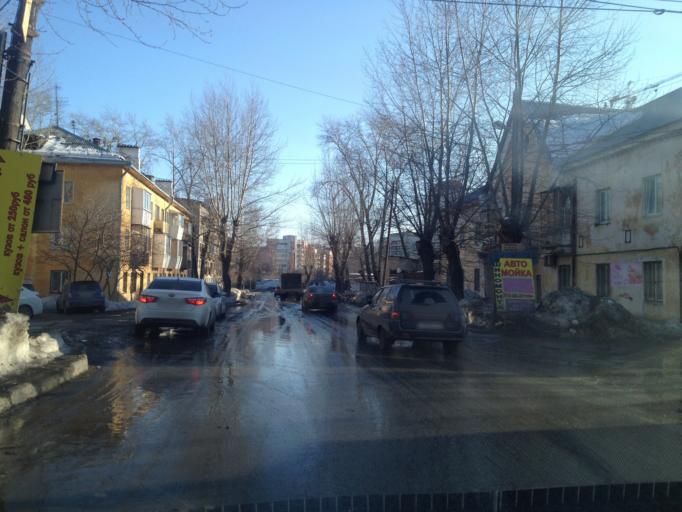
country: RU
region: Sverdlovsk
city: Yekaterinburg
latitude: 56.8578
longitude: 60.5810
